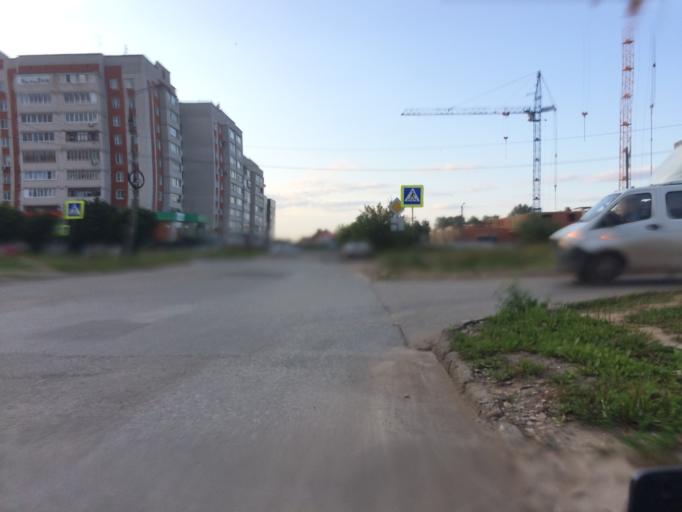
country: RU
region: Mariy-El
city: Medvedevo
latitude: 56.6443
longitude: 47.8447
